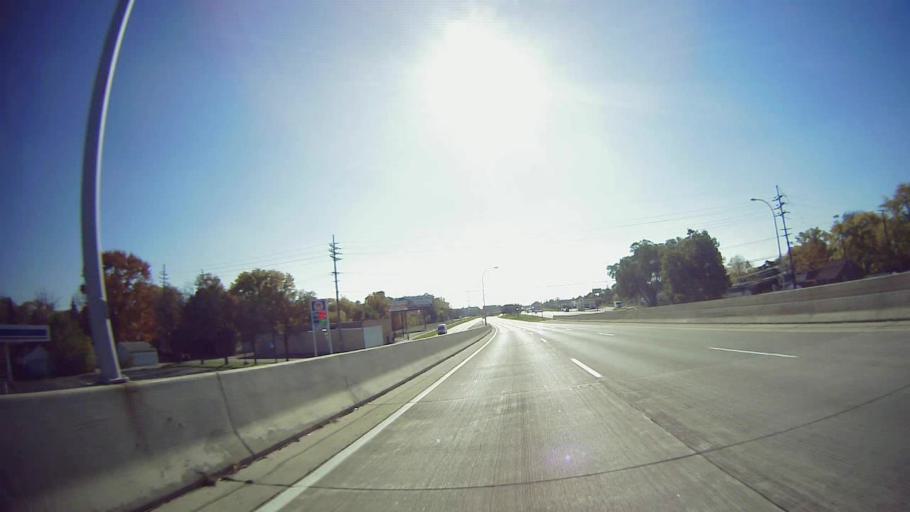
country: US
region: Michigan
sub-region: Wayne County
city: Redford
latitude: 42.3839
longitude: -83.2760
